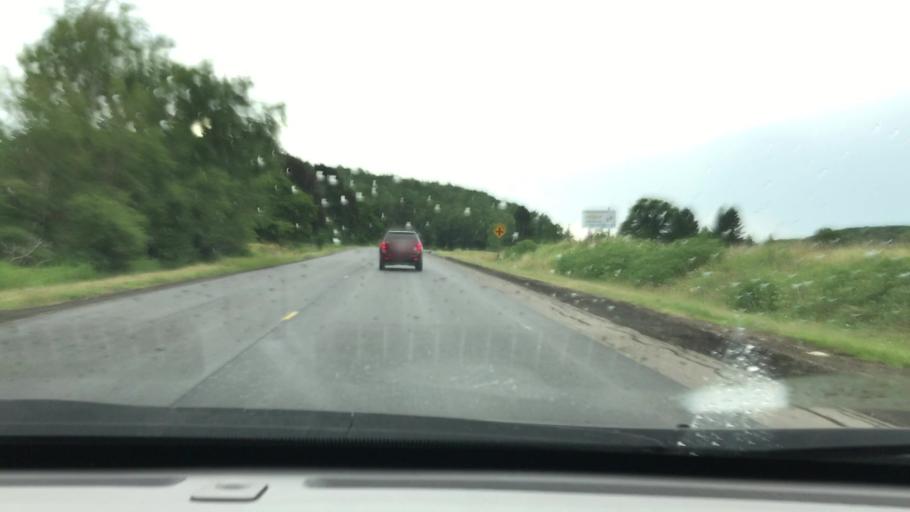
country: US
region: New York
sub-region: Erie County
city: Springville
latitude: 42.3618
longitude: -78.6545
